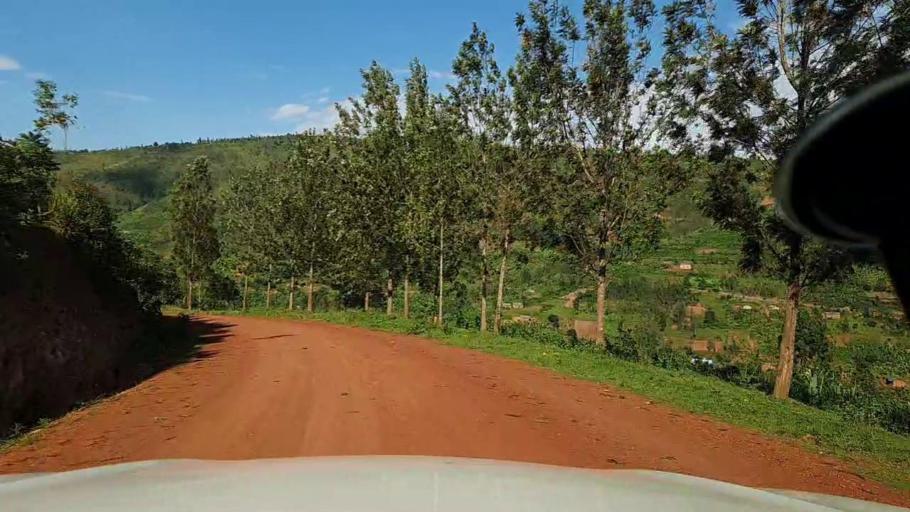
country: RW
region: Kigali
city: Kigali
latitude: -1.8480
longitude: 29.8652
